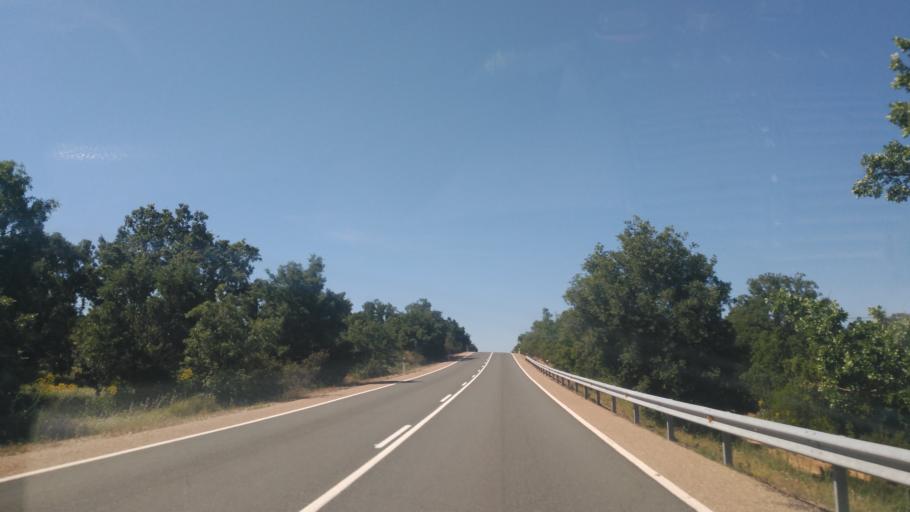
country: ES
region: Castille and Leon
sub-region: Provincia de Zamora
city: Cuelgamures
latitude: 41.2767
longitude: -5.7173
